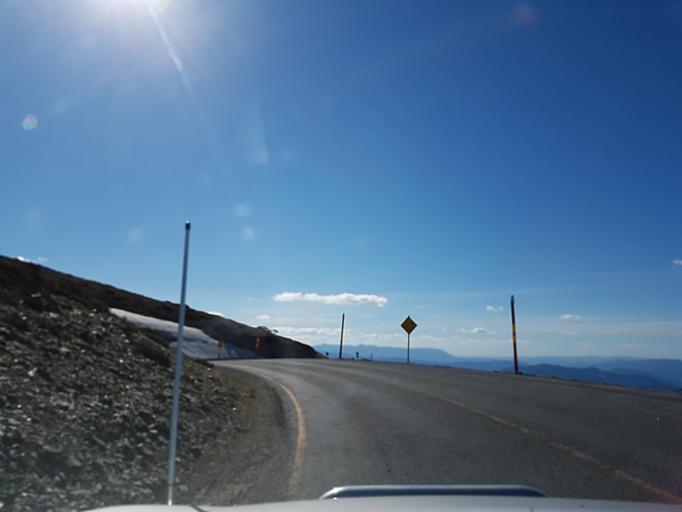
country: AU
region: Victoria
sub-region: Alpine
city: Mount Beauty
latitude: -36.9742
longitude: 147.1323
